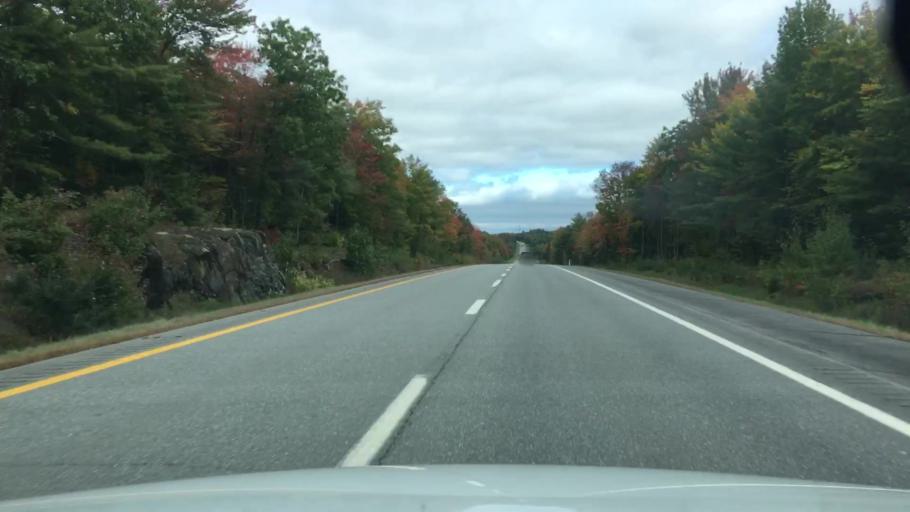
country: US
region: Maine
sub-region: Penobscot County
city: Carmel
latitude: 44.7776
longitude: -69.0585
